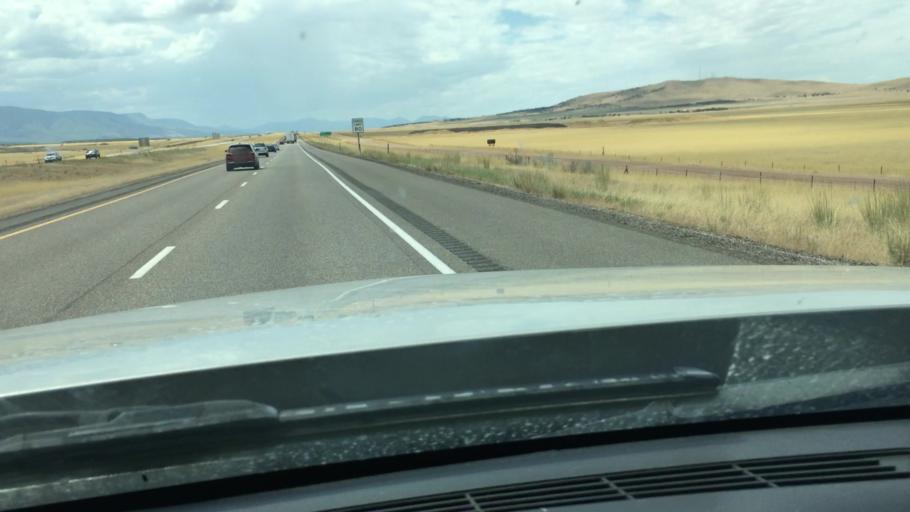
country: US
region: Utah
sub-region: Millard County
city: Fillmore
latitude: 39.0716
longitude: -112.2820
